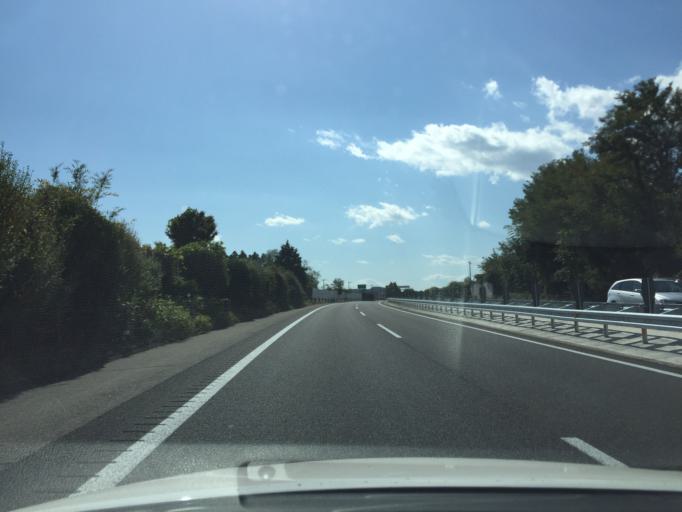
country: JP
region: Fukushima
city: Sukagawa
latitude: 37.2064
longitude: 140.3074
